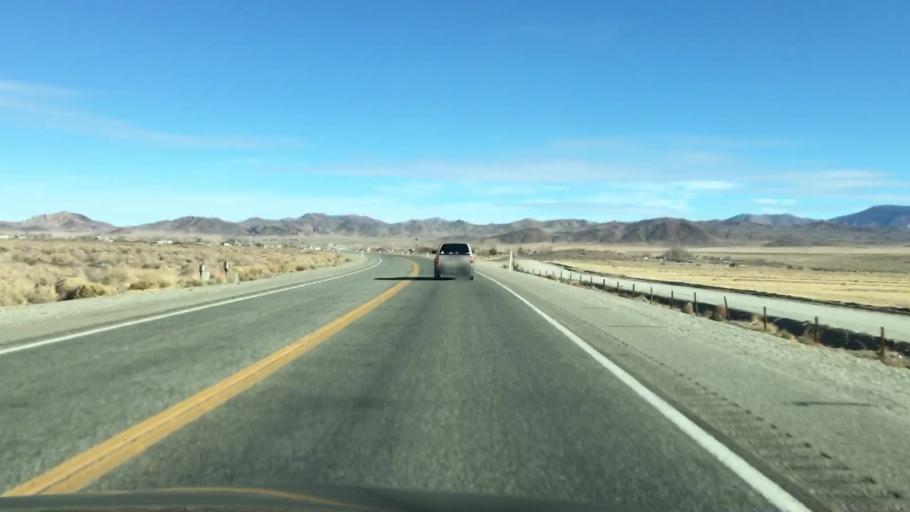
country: US
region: Nevada
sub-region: Lyon County
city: Yerington
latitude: 38.9976
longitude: -119.1062
